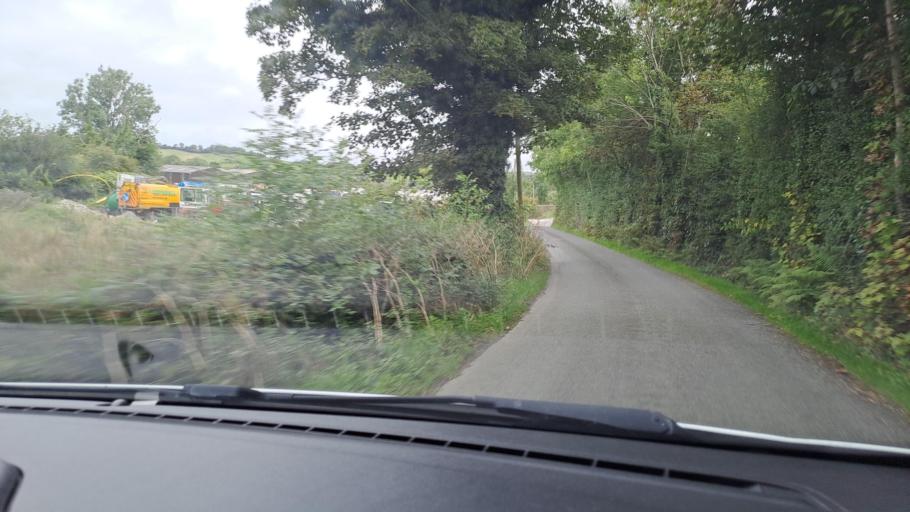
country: IE
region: Ulster
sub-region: County Monaghan
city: Carrickmacross
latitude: 54.0324
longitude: -6.8144
